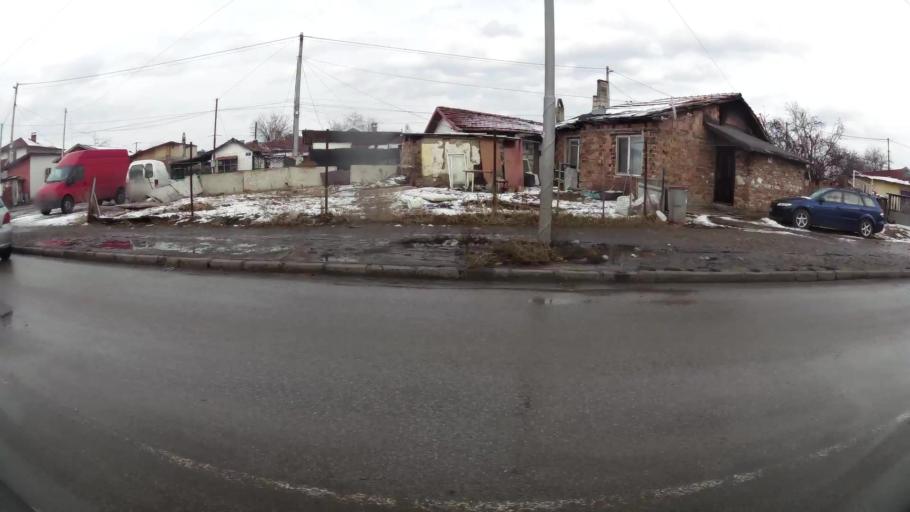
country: BG
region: Sofia-Capital
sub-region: Stolichna Obshtina
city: Sofia
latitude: 42.6931
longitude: 23.3833
